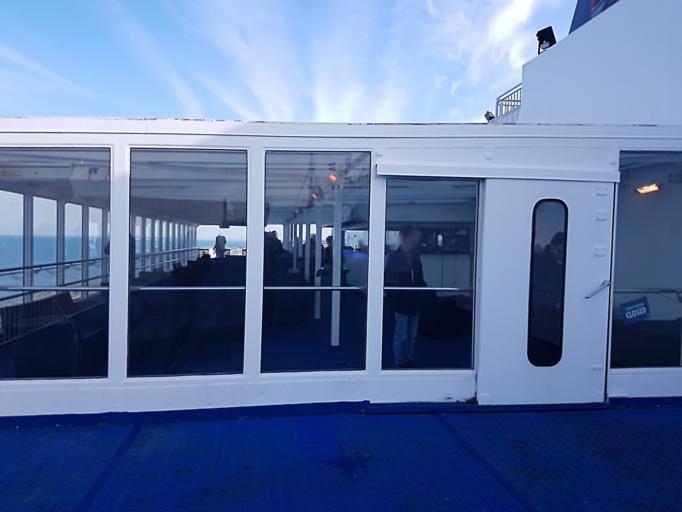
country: DK
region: North Denmark
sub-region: Hjorring Kommune
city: Hirtshals
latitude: 57.5960
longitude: 9.9743
